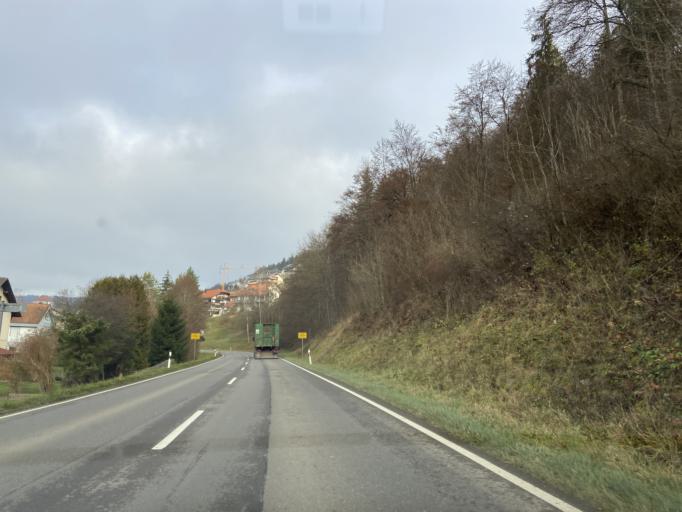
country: DE
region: Baden-Wuerttemberg
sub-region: Tuebingen Region
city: Hettingen
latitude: 48.2097
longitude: 9.2297
